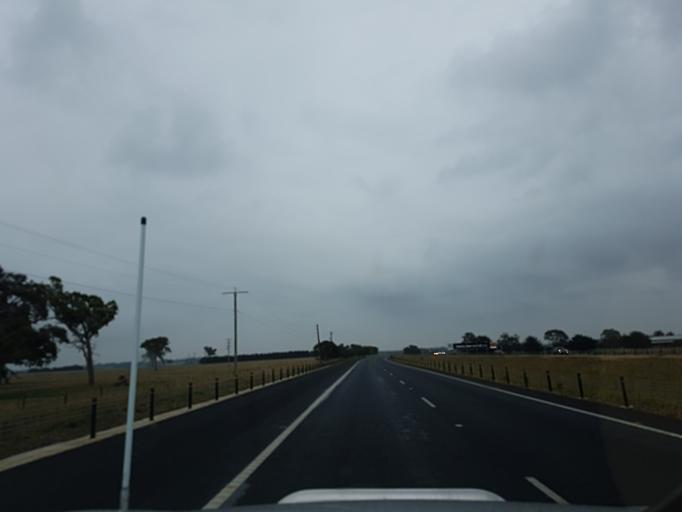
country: AU
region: Victoria
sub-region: Wellington
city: Heyfield
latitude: -38.1591
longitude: 146.7283
